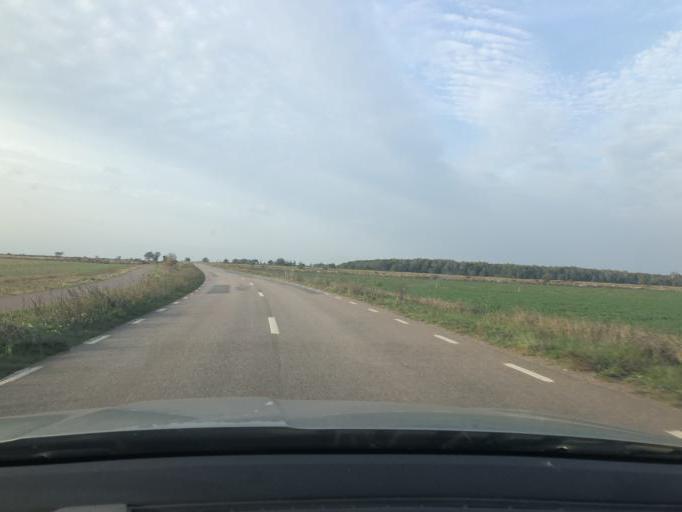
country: SE
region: Kalmar
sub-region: Morbylanga Kommun
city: Moerbylanga
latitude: 56.3040
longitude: 16.4110
